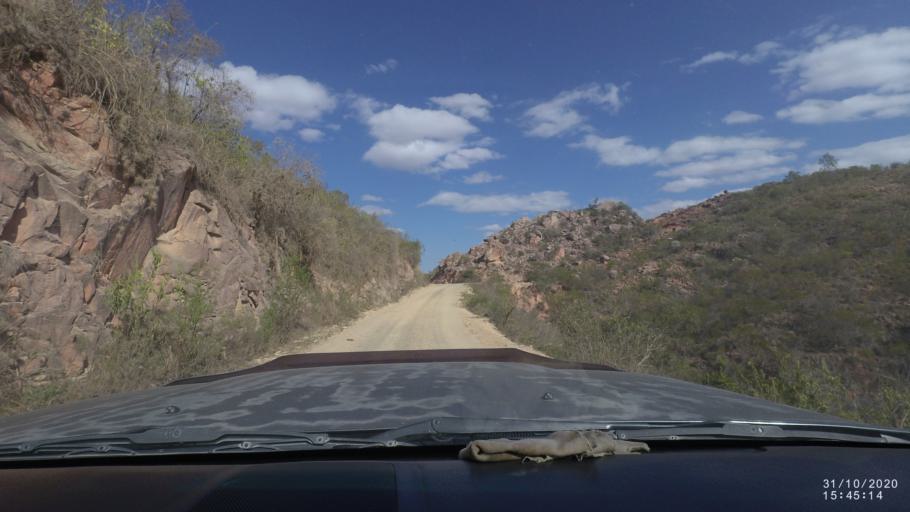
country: BO
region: Chuquisaca
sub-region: Provincia Zudanez
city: Mojocoya
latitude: -18.3188
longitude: -64.7179
